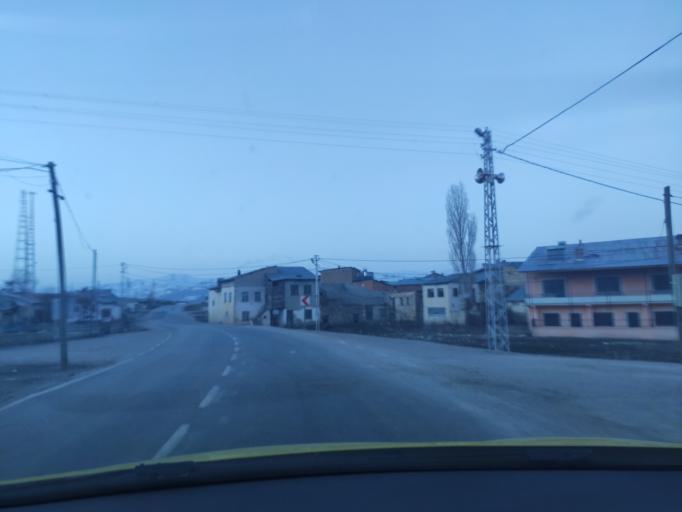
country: TR
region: Bayburt
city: Aydintepe
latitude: 40.3358
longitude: 40.1262
